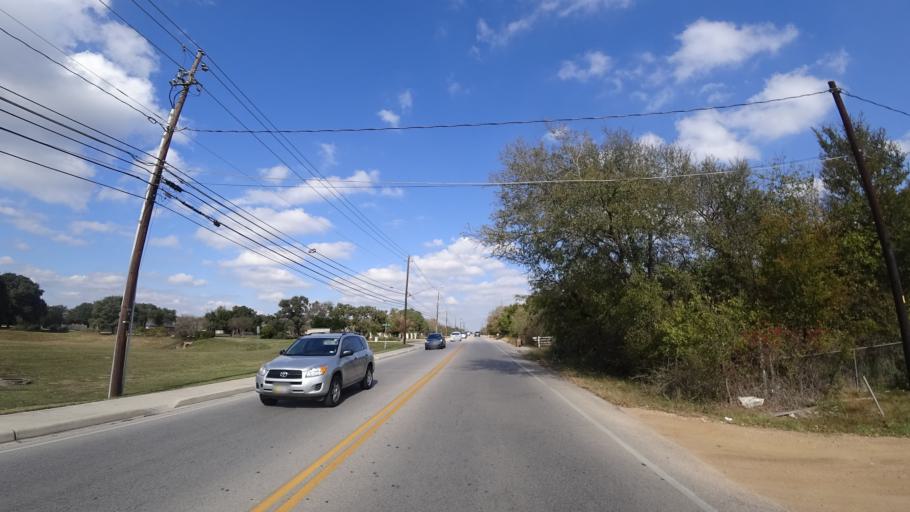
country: US
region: Texas
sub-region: Travis County
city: Shady Hollow
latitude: 30.1787
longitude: -97.8529
